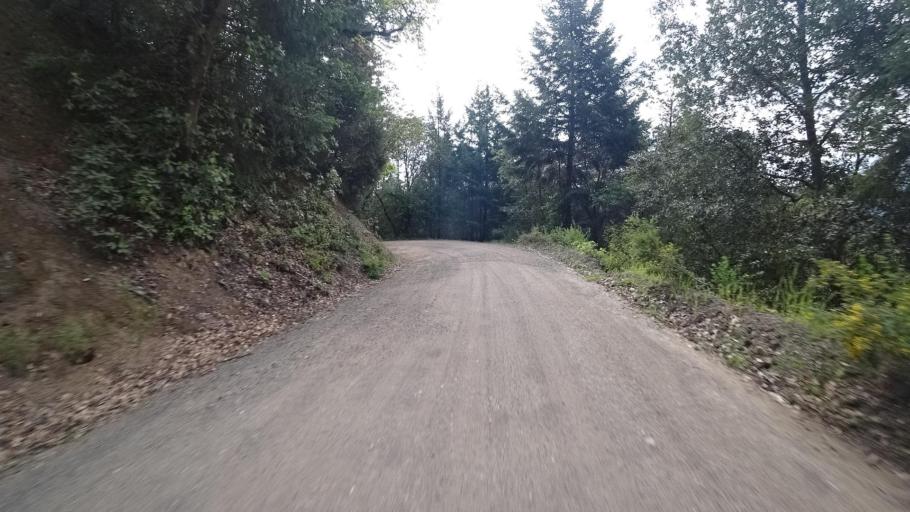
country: US
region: California
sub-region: Humboldt County
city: Redway
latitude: 40.2104
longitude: -123.6714
